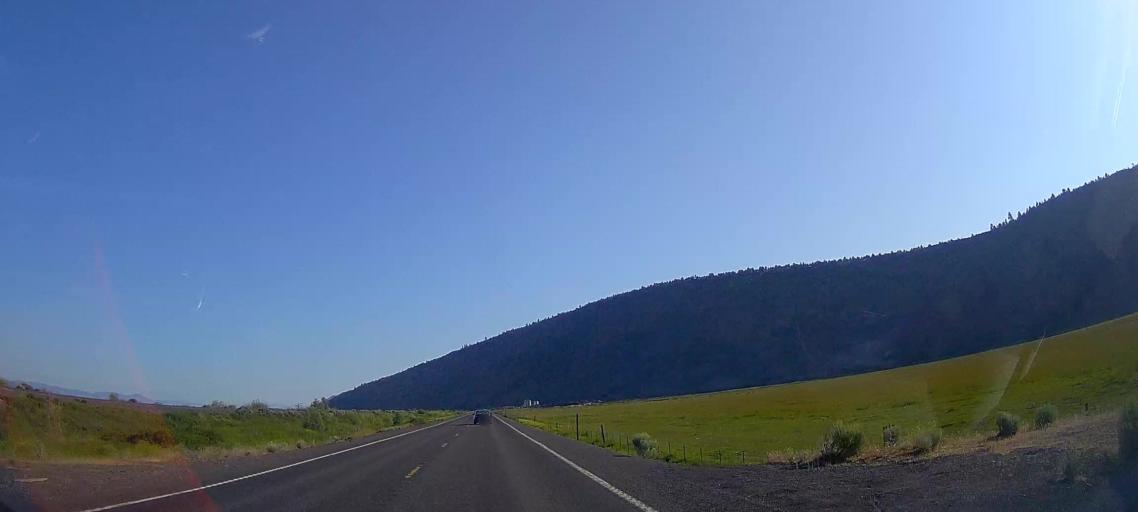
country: US
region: Oregon
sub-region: Klamath County
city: Klamath Falls
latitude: 42.3125
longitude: -121.8174
